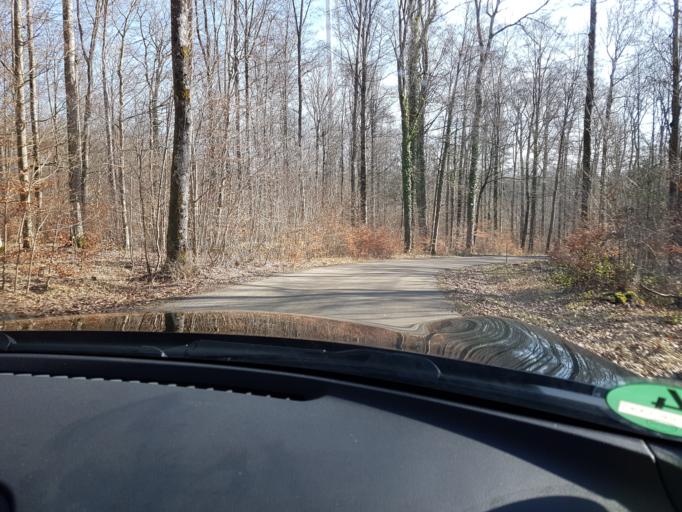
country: DE
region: Baden-Wuerttemberg
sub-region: Regierungsbezirk Stuttgart
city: Langenburg
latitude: 49.2870
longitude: 9.8773
